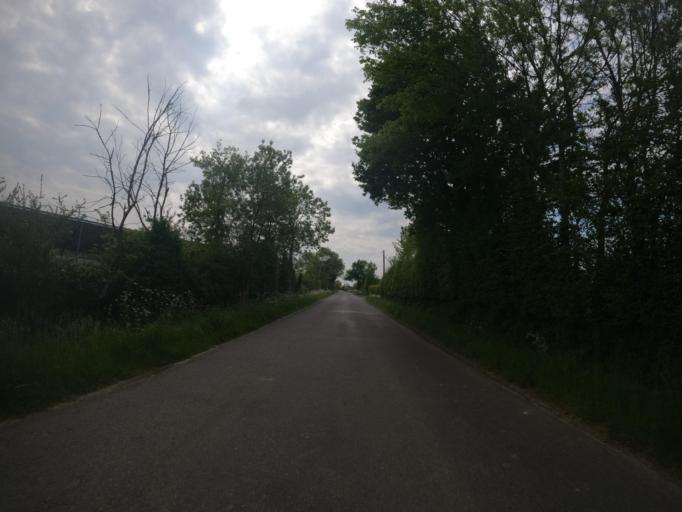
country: FR
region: Poitou-Charentes
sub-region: Departement des Deux-Sevres
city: Saint-Varent
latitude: 46.8773
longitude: -0.2774
